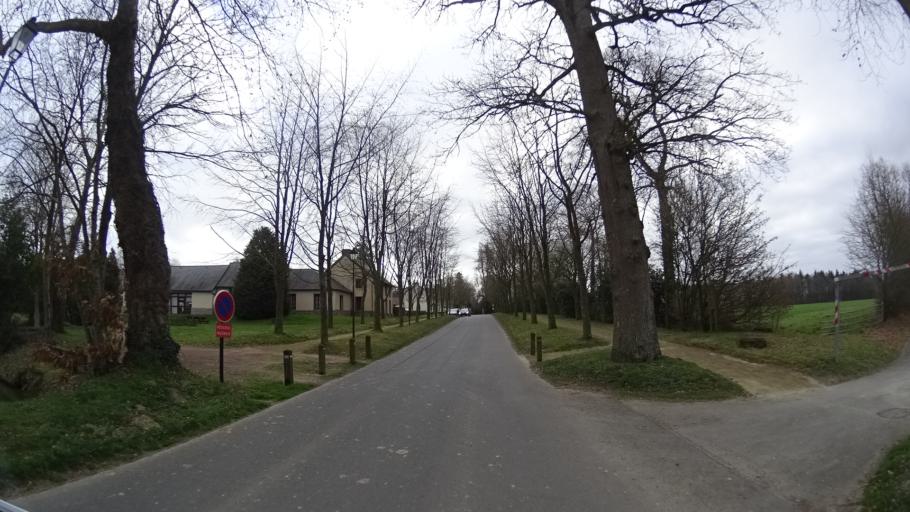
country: FR
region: Brittany
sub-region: Departement d'Ille-et-Vilaine
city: Saint-Gilles
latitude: 48.1760
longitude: -1.8547
